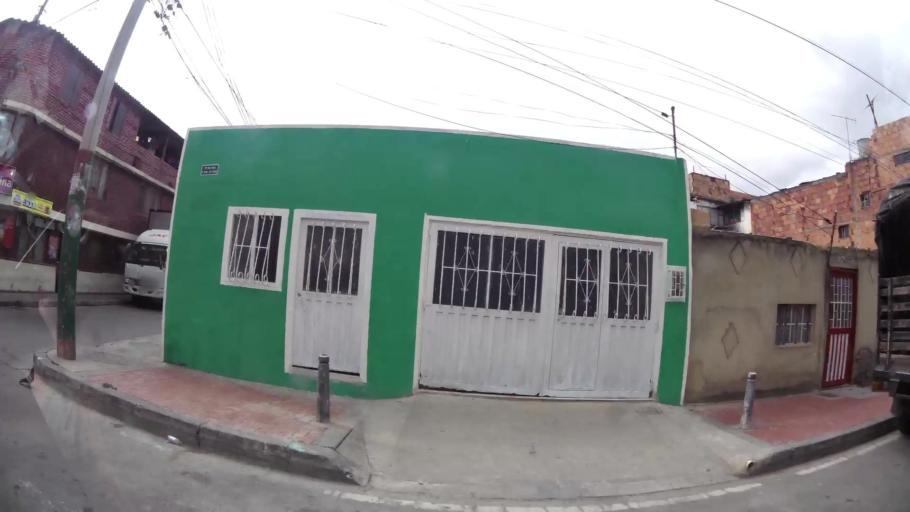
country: CO
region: Bogota D.C.
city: Bogota
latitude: 4.6049
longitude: -74.1412
